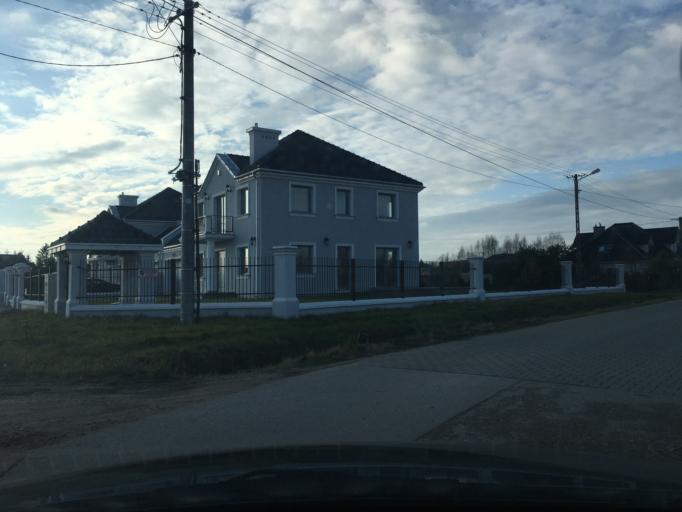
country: PL
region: Masovian Voivodeship
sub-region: Powiat piaseczynski
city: Lesznowola
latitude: 52.0256
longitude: 20.9444
